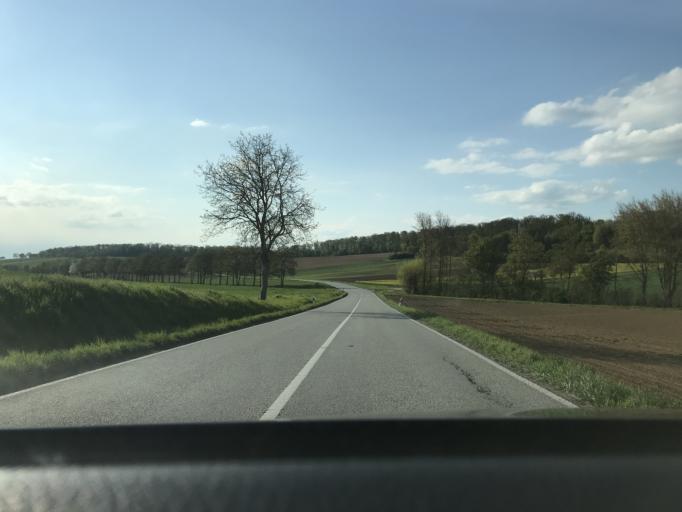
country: DE
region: Baden-Wuerttemberg
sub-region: Regierungsbezirk Stuttgart
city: Gemmingen
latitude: 49.1647
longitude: 8.9768
